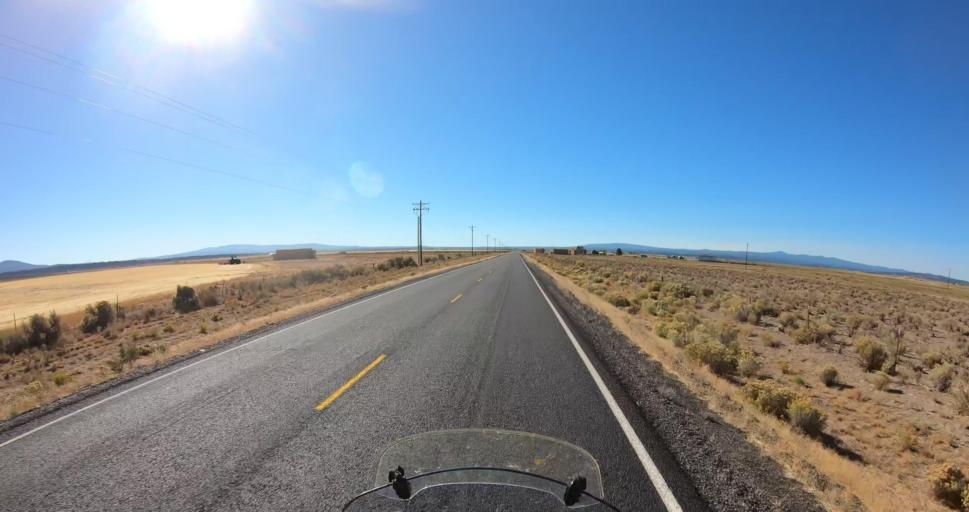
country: US
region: Oregon
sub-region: Deschutes County
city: La Pine
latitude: 43.1285
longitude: -120.9705
